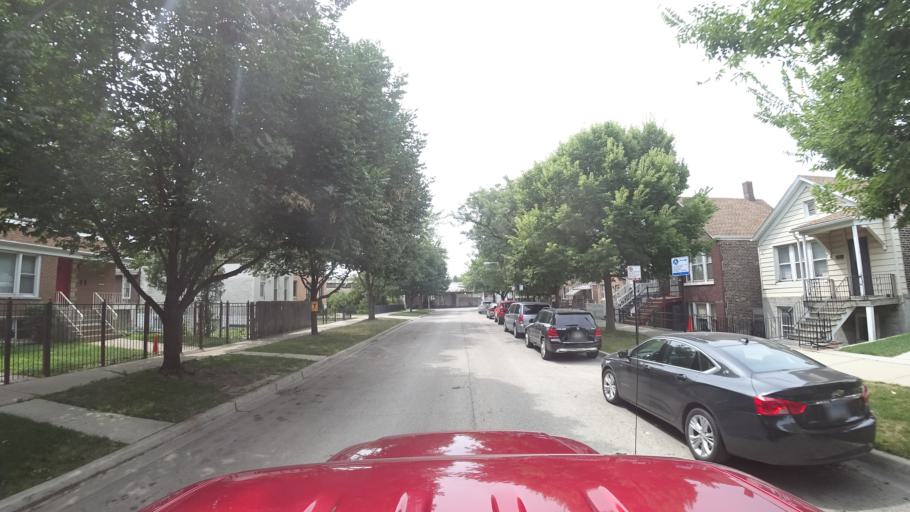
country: US
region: Illinois
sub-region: Cook County
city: Chicago
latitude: 41.8331
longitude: -87.6766
